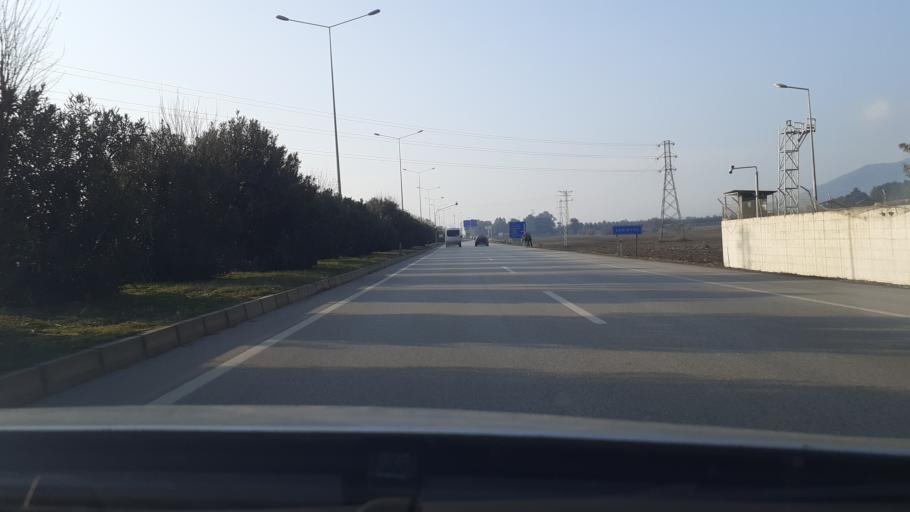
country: TR
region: Hatay
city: Serinyol
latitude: 36.3763
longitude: 36.2273
